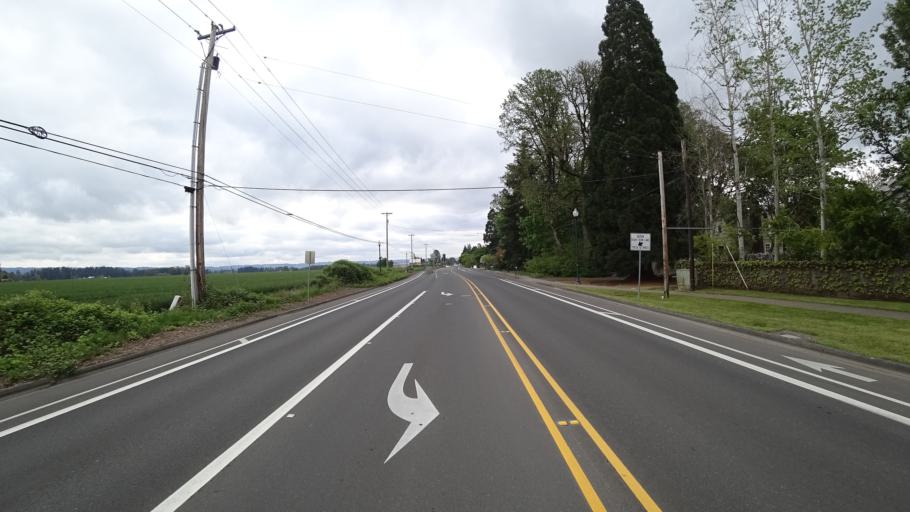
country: US
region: Oregon
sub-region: Washington County
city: Hillsboro
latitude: 45.5499
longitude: -122.9861
